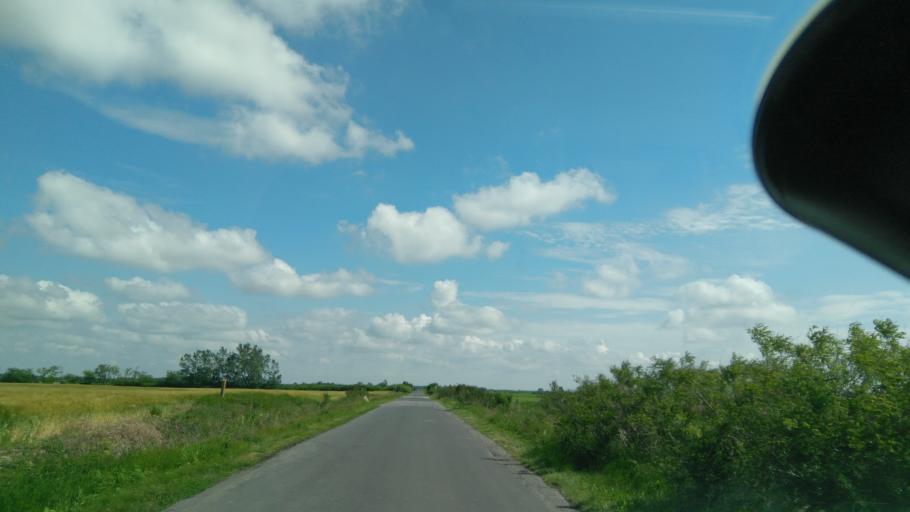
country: HU
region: Bekes
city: Bekes
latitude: 46.8109
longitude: 21.1467
